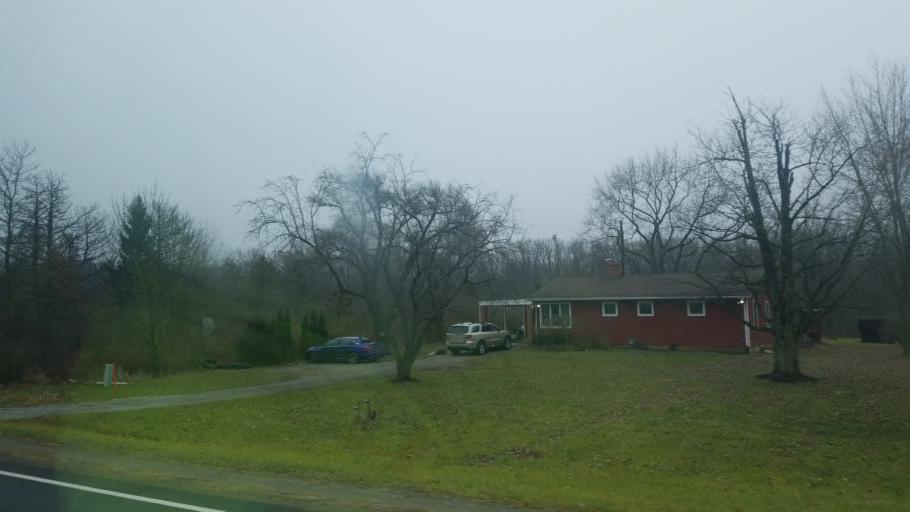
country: US
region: Ohio
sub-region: Union County
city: Marysville
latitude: 40.2472
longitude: -83.4118
